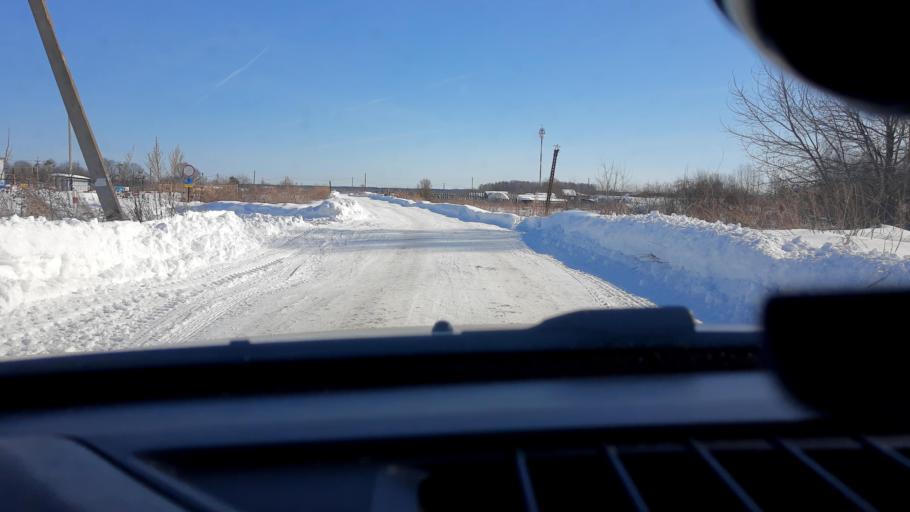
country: RU
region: Nizjnij Novgorod
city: Volodarsk
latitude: 56.2463
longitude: 43.1855
